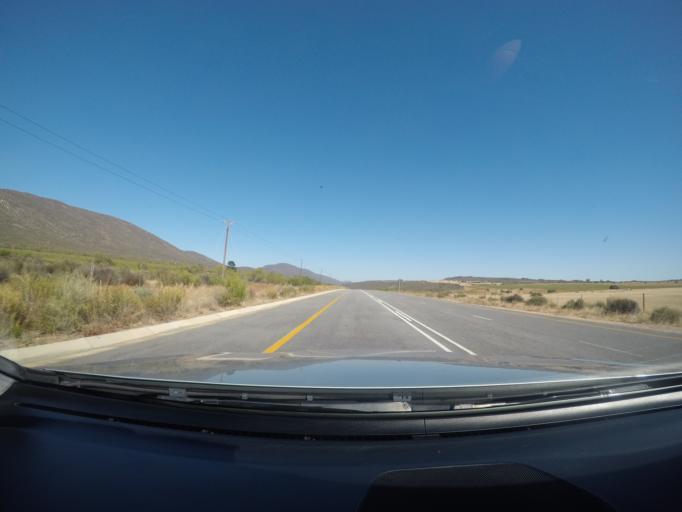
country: ZA
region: Western Cape
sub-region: West Coast District Municipality
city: Clanwilliam
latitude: -32.2722
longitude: 18.8815
